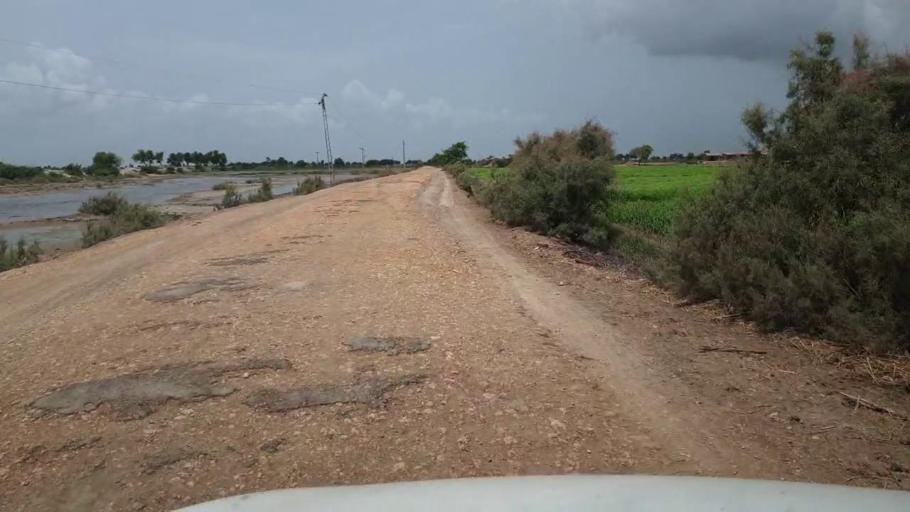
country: PK
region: Sindh
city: Kario
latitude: 24.7520
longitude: 68.4578
